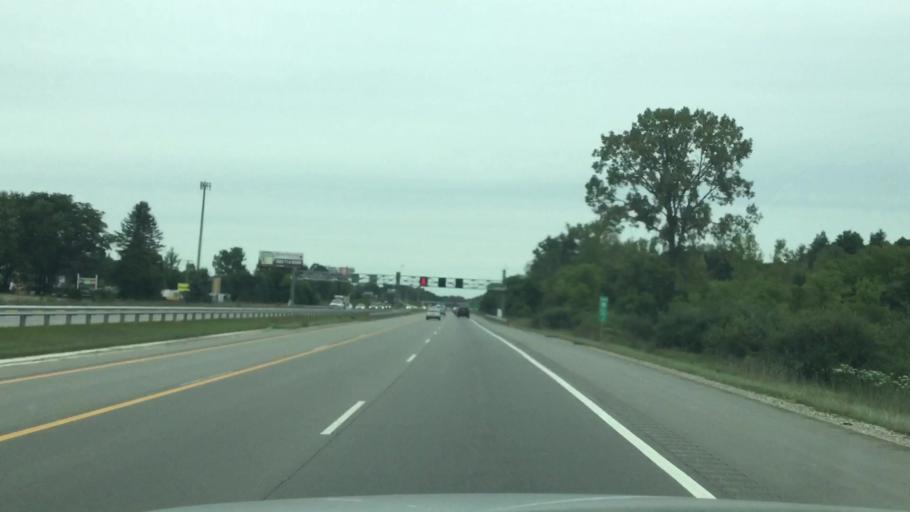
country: US
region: Michigan
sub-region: Livingston County
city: Whitmore Lake
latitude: 42.3702
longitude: -83.7513
